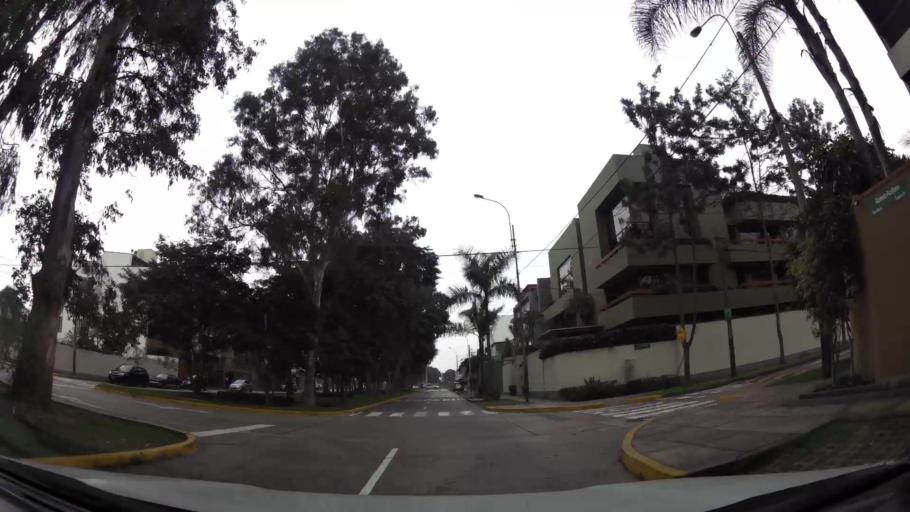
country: PE
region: Lima
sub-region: Lima
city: San Luis
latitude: -12.1047
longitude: -76.9828
